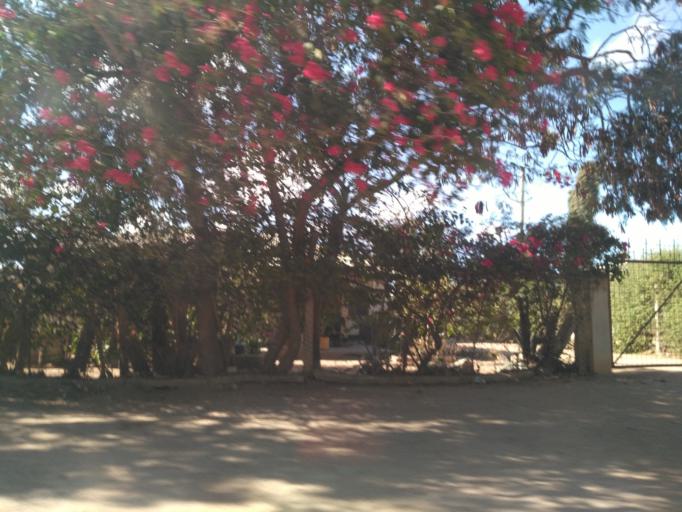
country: TZ
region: Dodoma
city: Dodoma
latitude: -6.1854
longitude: 35.7396
